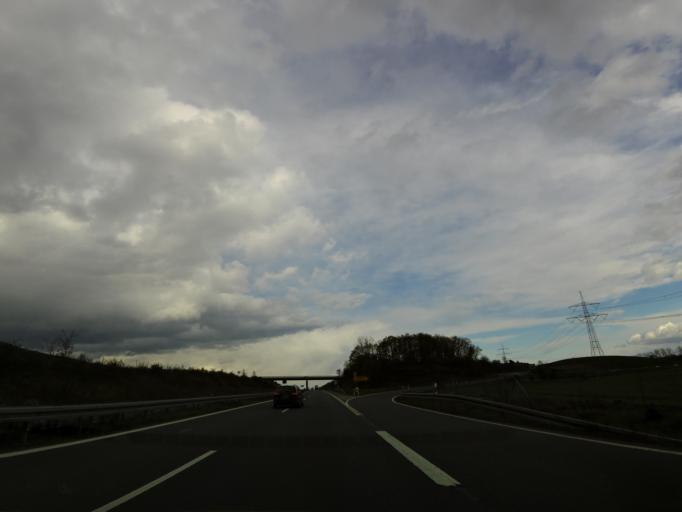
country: DE
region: Saxony-Anhalt
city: Quedlinburg
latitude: 51.8116
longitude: 11.1241
